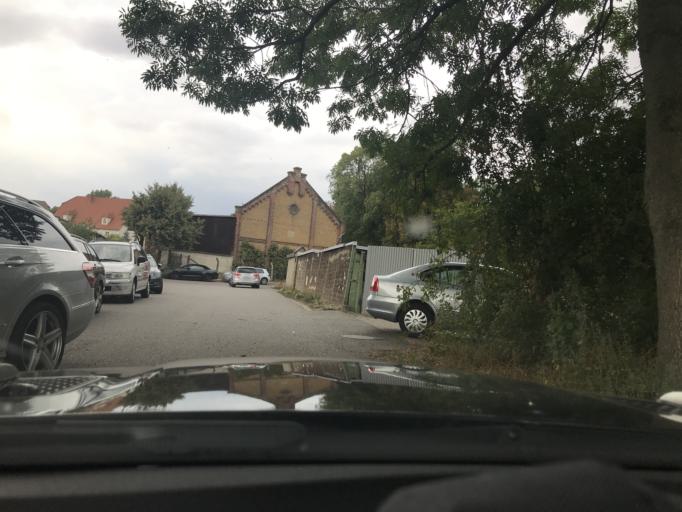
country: DE
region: Saxony-Anhalt
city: Landsberg
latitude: 51.5367
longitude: 12.1384
